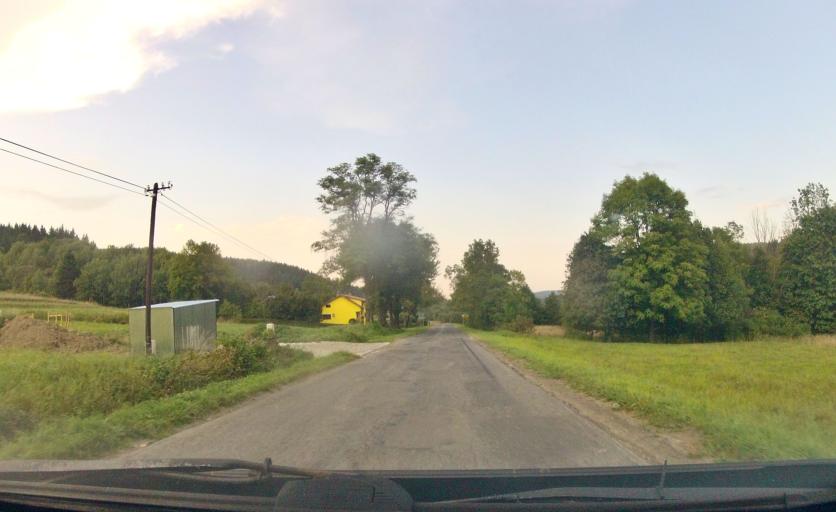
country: PL
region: Subcarpathian Voivodeship
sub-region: Powiat krosnienski
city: Dukla
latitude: 49.5393
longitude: 21.6163
